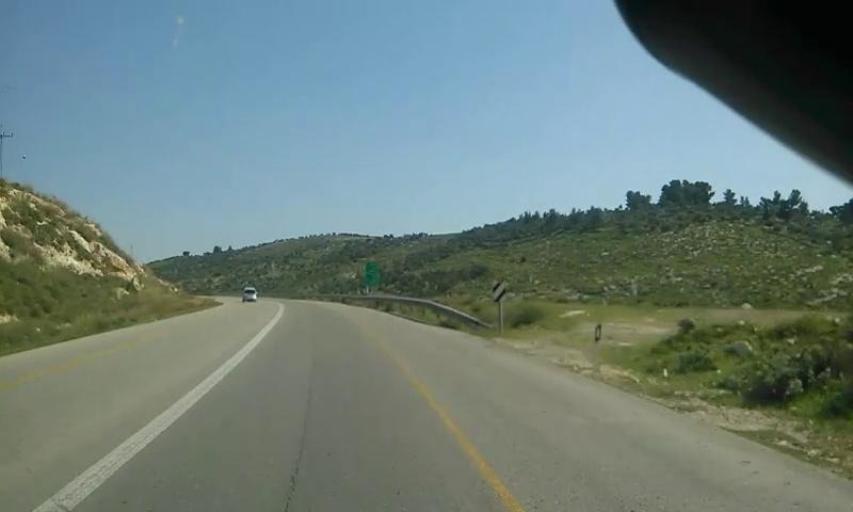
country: PS
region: West Bank
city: Tarqumya
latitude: 31.5648
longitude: 34.9957
